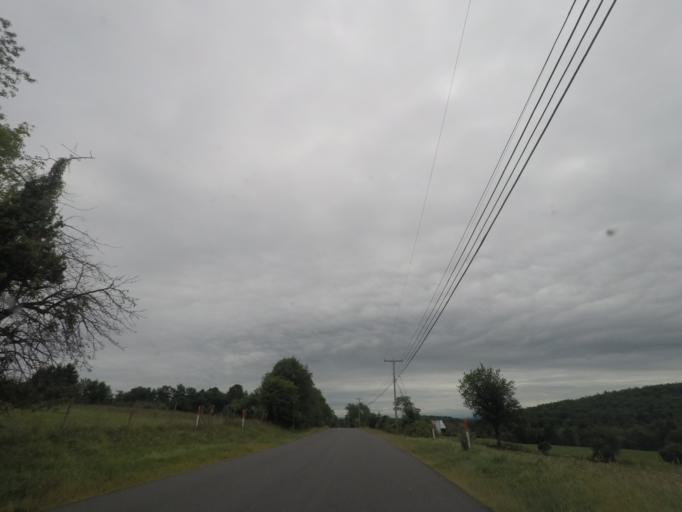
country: US
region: New York
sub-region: Rensselaer County
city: Nassau
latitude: 42.4962
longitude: -73.6033
